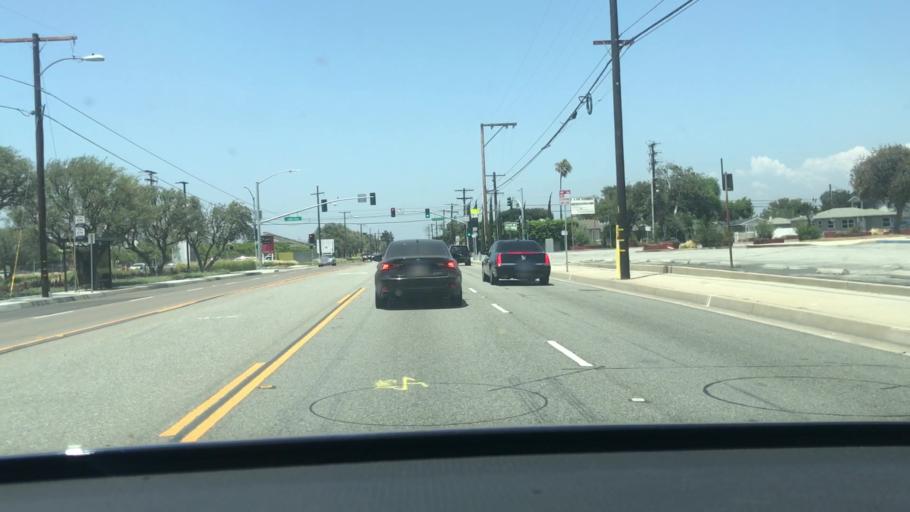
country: US
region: California
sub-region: Los Angeles County
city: Del Aire
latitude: 33.9086
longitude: -118.3787
